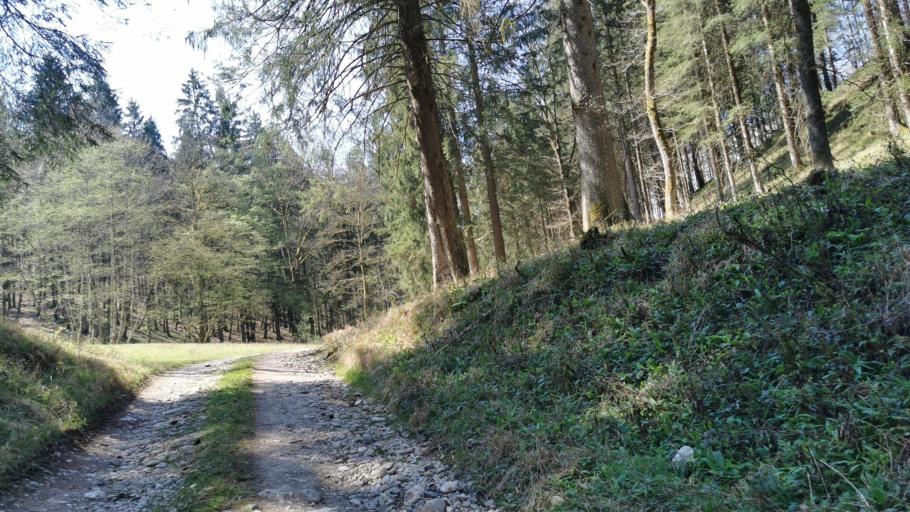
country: AT
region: Salzburg
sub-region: Politischer Bezirk Salzburg-Umgebung
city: Grodig
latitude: 47.7451
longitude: 13.0006
